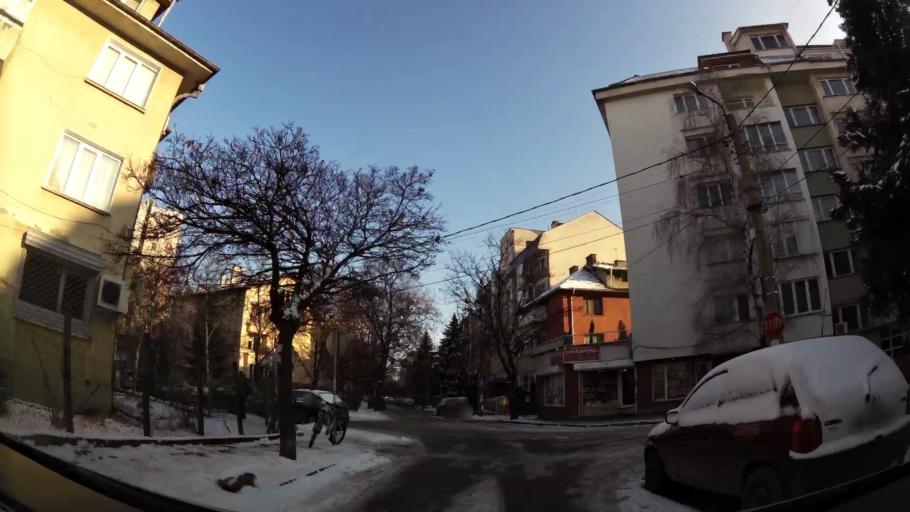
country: BG
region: Sofia-Capital
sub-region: Stolichna Obshtina
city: Sofia
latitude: 42.6766
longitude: 23.3625
